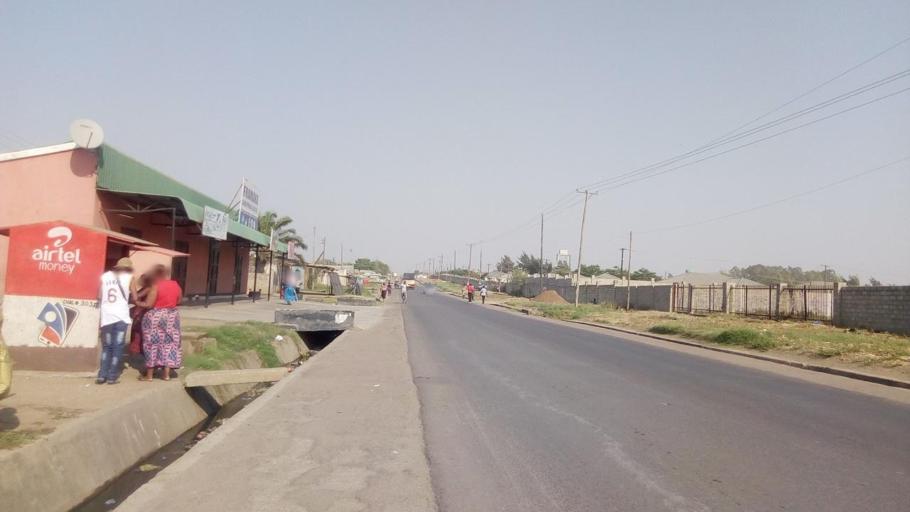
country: ZM
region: Lusaka
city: Lusaka
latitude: -15.3692
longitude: 28.2867
